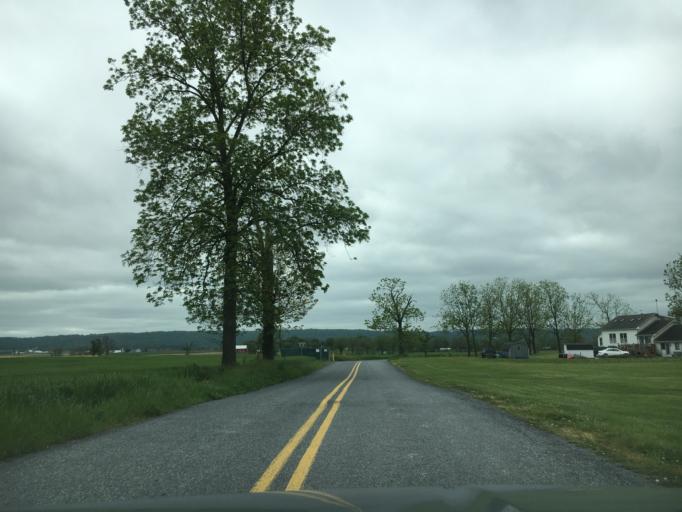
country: US
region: Pennsylvania
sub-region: Berks County
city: Fleetwood
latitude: 40.4862
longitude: -75.8319
